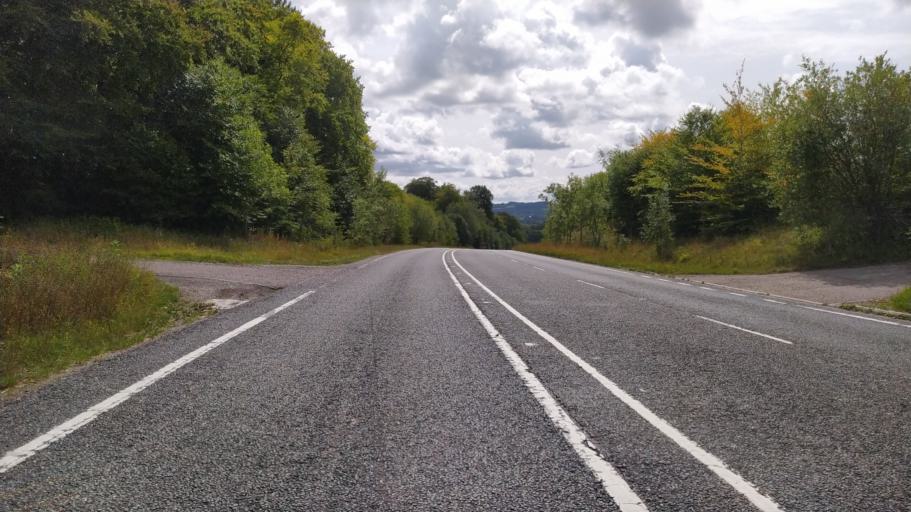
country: GB
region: England
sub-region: Wiltshire
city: Hindon
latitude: 51.0834
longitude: -2.1657
